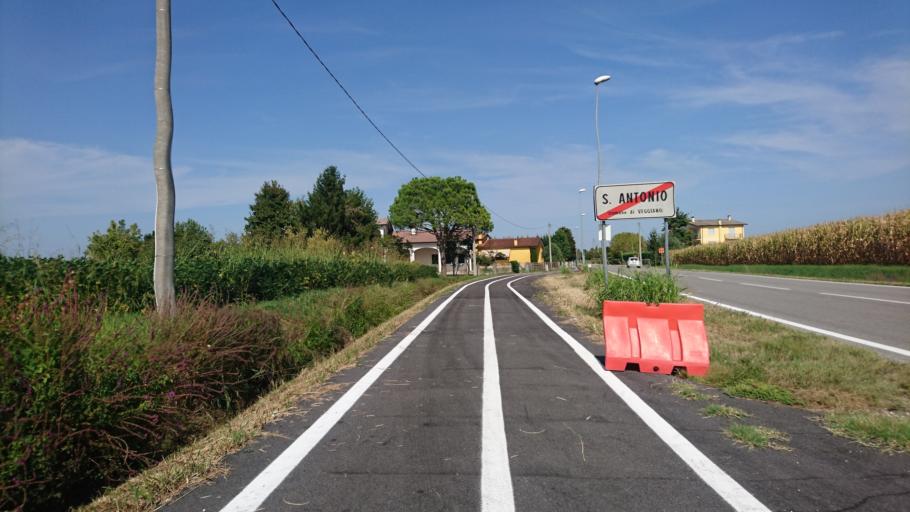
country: IT
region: Veneto
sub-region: Provincia di Padova
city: Veggiano
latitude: 45.4402
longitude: 11.7013
